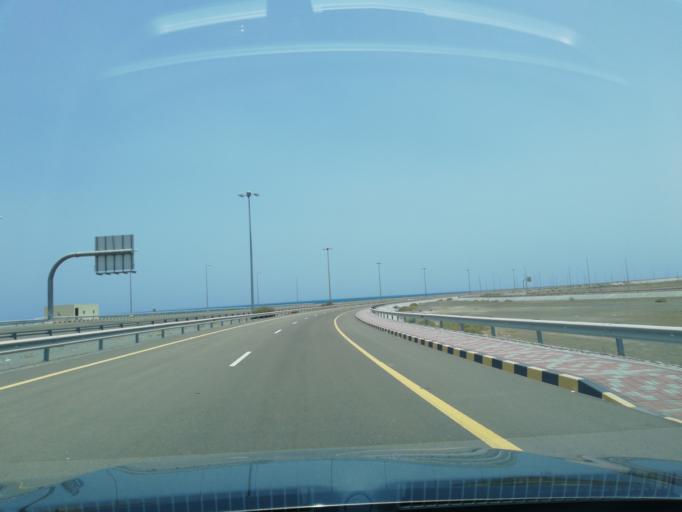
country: AE
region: Al Fujayrah
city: Al Fujayrah
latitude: 24.9530
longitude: 56.3772
